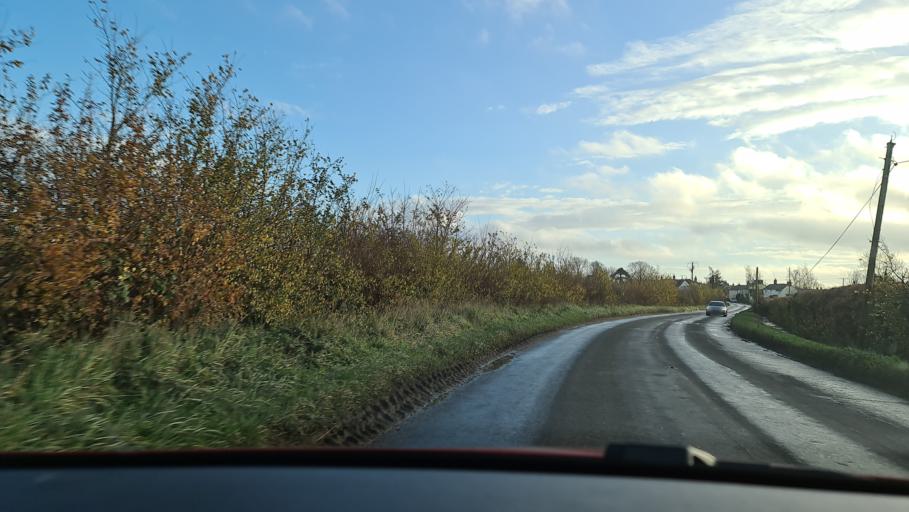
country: GB
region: England
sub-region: Buckinghamshire
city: Haddenham
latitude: 51.7933
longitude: -0.9368
